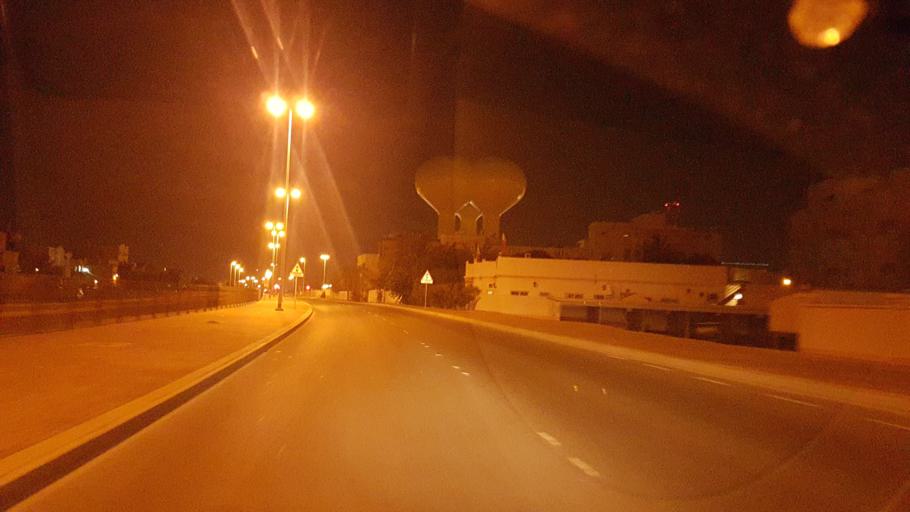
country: BH
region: Muharraq
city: Al Hadd
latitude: 26.2476
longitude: 50.6522
